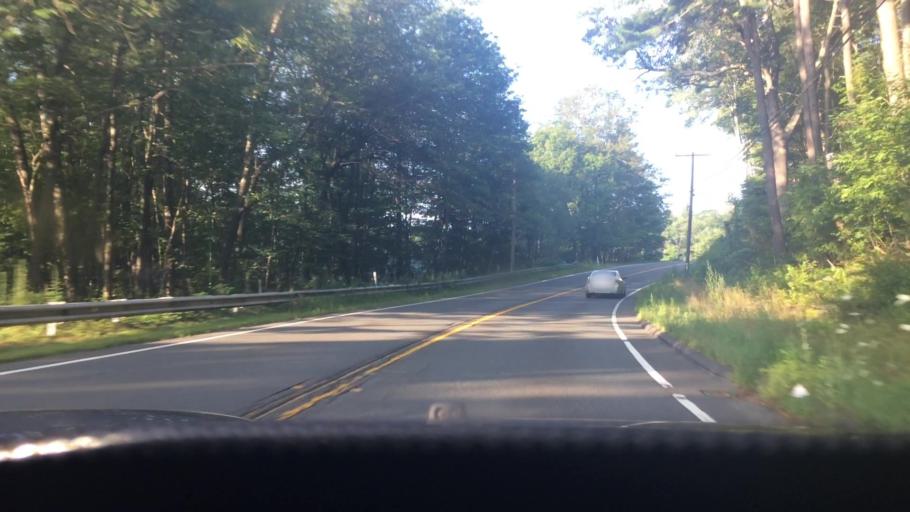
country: US
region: Massachusetts
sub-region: Franklin County
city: Erving
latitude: 42.5943
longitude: -72.4422
